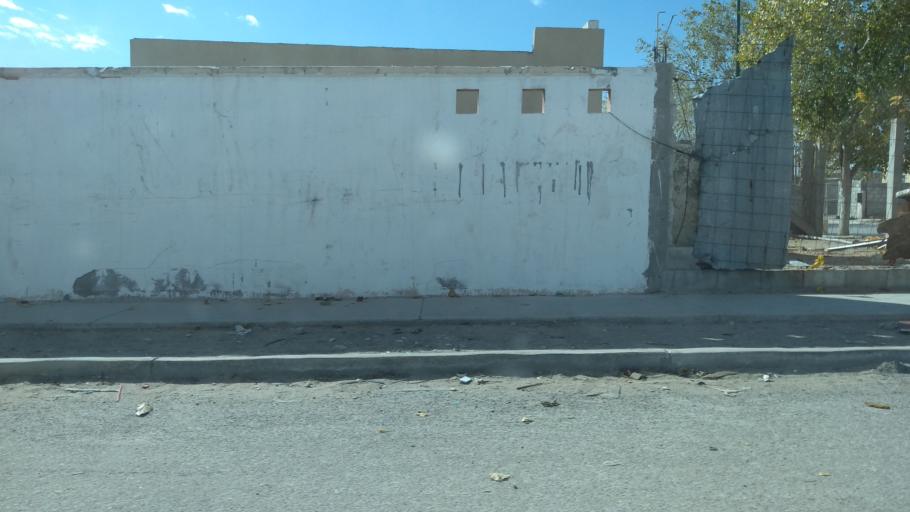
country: US
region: Texas
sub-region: El Paso County
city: Socorro Mission Number 1 Colonia
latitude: 31.5863
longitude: -106.3584
